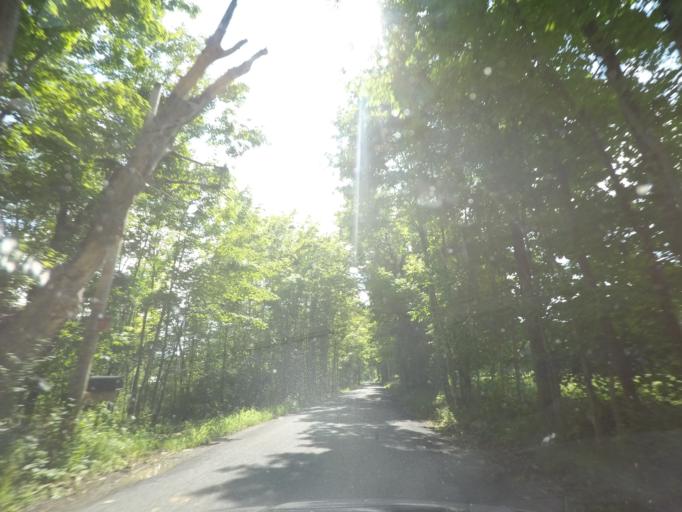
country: US
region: New York
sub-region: Rensselaer County
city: Averill Park
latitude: 42.5792
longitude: -73.5335
